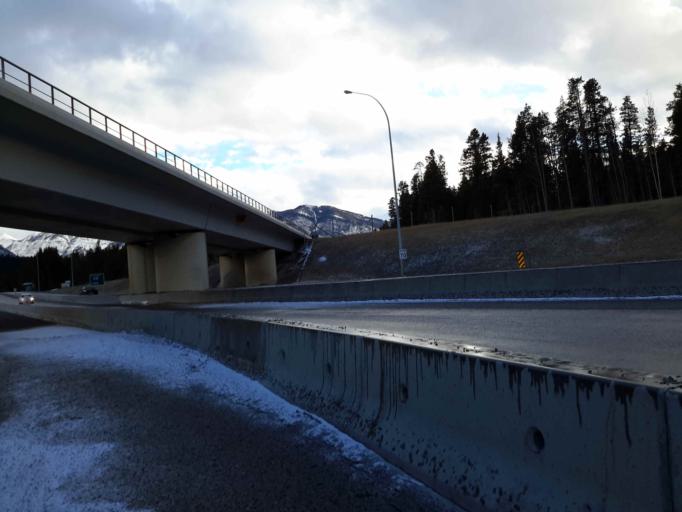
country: CA
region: Alberta
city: Banff
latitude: 51.2065
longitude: -115.5372
